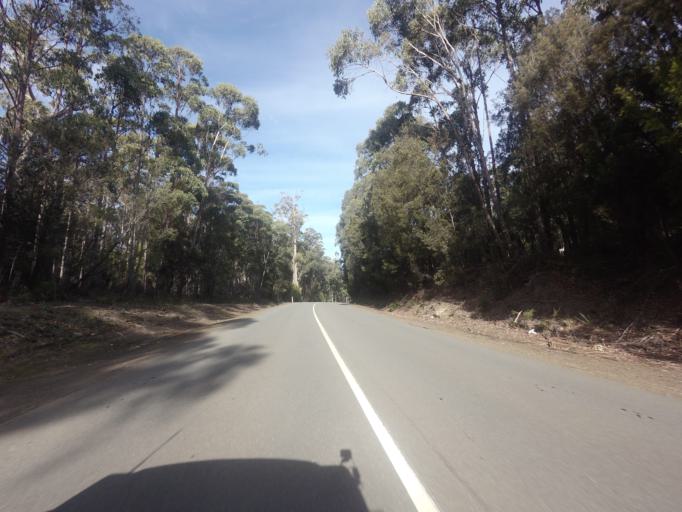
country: AU
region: Tasmania
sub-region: Clarence
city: Sandford
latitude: -43.0575
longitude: 147.8518
